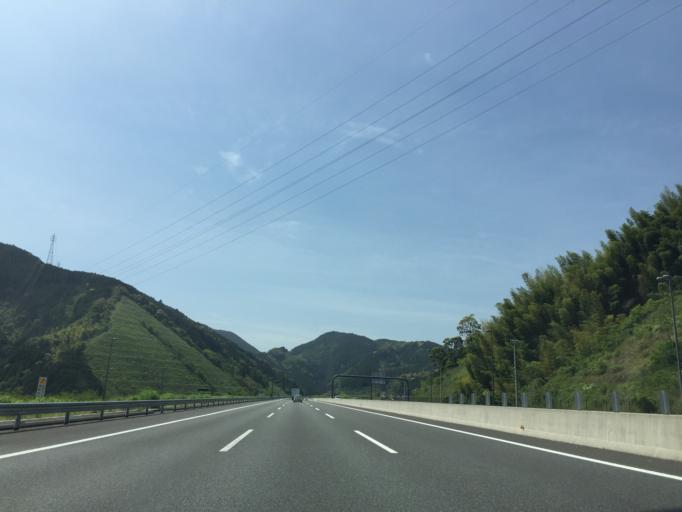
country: JP
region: Shizuoka
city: Shizuoka-shi
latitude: 34.9751
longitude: 138.2935
